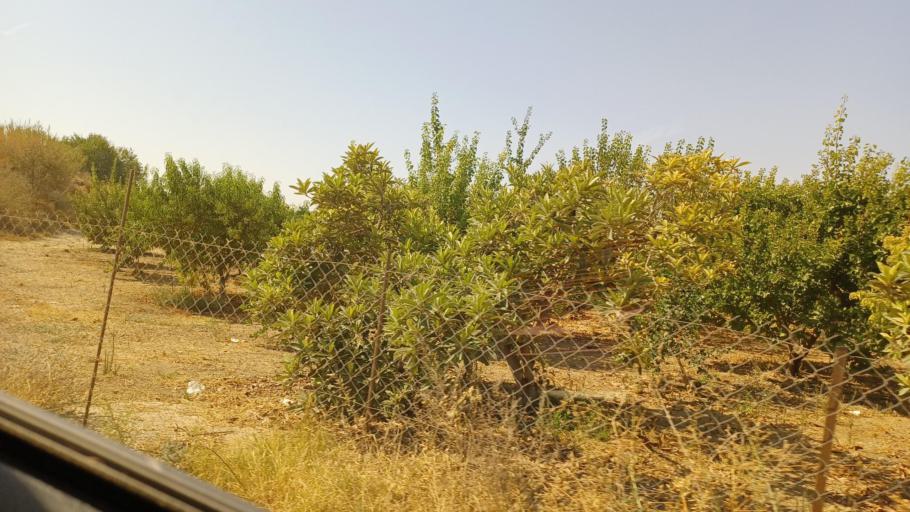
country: CY
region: Pafos
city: Polis
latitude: 35.0489
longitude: 32.4451
